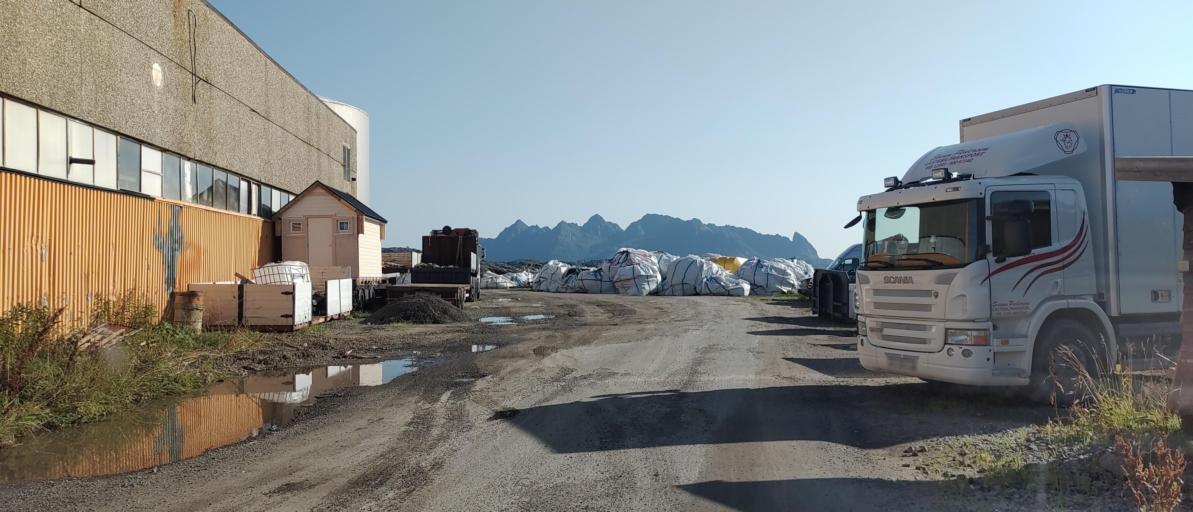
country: NO
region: Nordland
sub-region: Vagan
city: Svolvaer
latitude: 68.2291
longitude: 14.5728
